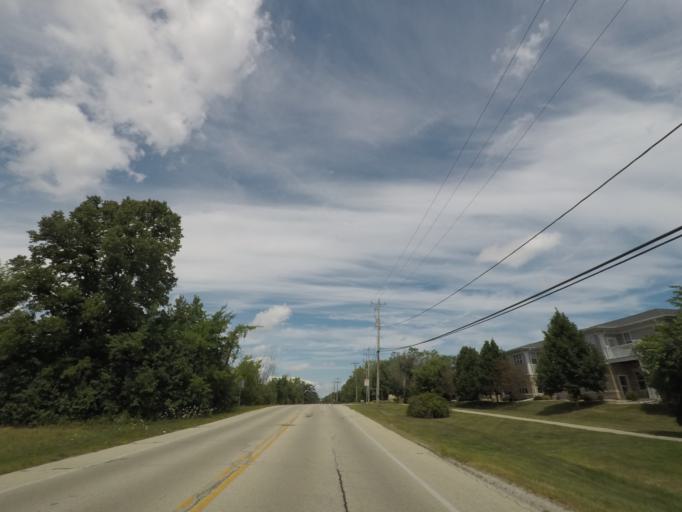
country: US
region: Wisconsin
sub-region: Milwaukee County
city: Greendale
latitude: 42.9049
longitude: -87.9799
